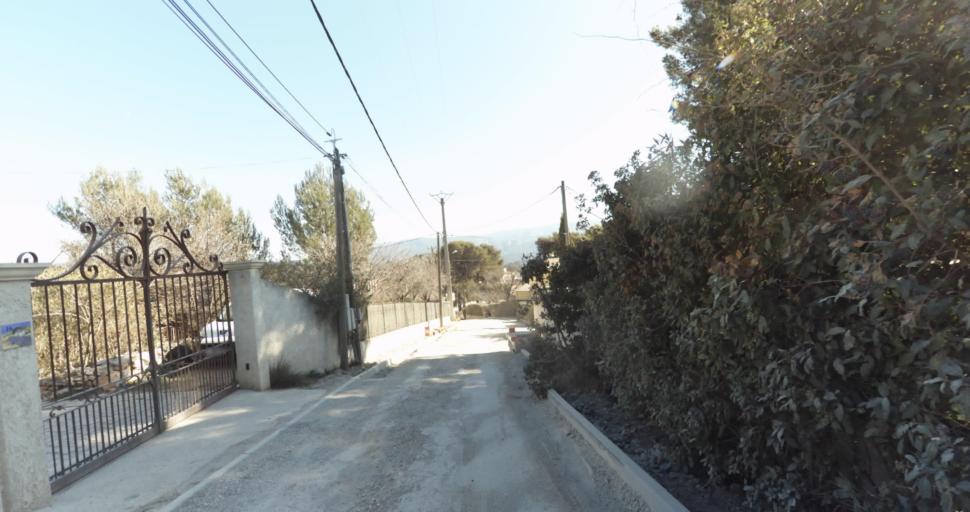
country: FR
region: Provence-Alpes-Cote d'Azur
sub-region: Departement des Bouches-du-Rhone
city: Peypin
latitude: 43.3864
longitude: 5.5736
